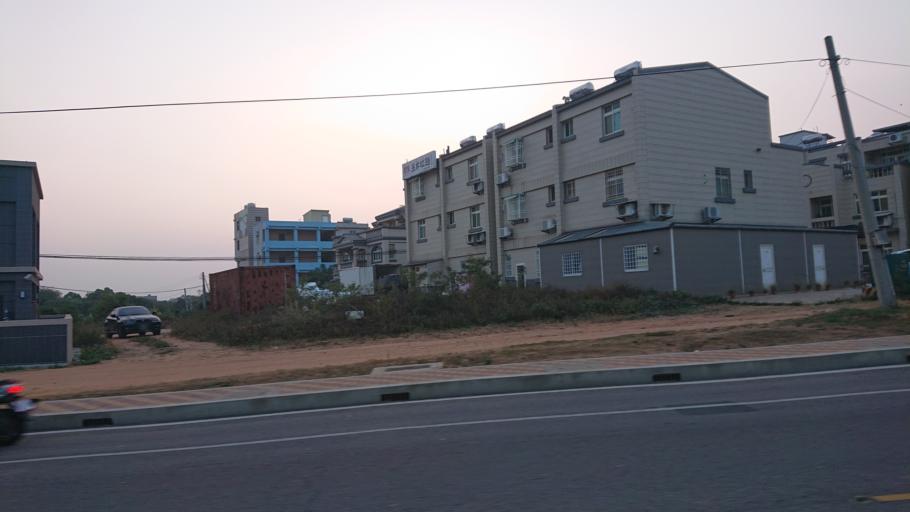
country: TW
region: Fukien
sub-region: Kinmen
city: Jincheng
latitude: 24.4418
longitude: 118.3205
